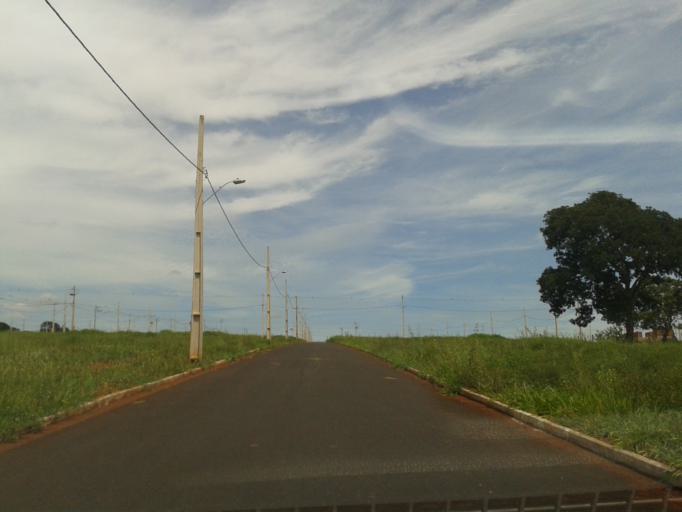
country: BR
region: Minas Gerais
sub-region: Santa Vitoria
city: Santa Vitoria
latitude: -18.8398
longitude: -50.1351
